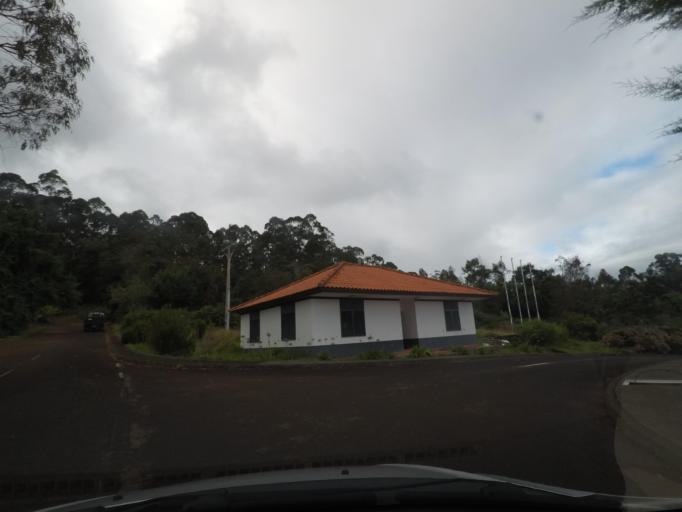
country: PT
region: Madeira
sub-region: Santana
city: Santana
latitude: 32.7860
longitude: -16.8802
